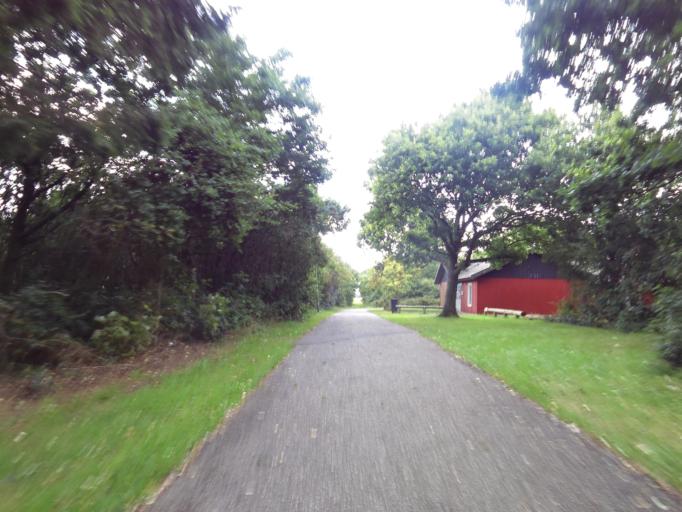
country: DK
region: South Denmark
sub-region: Esbjerg Kommune
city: Ribe
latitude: 55.3158
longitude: 8.7434
